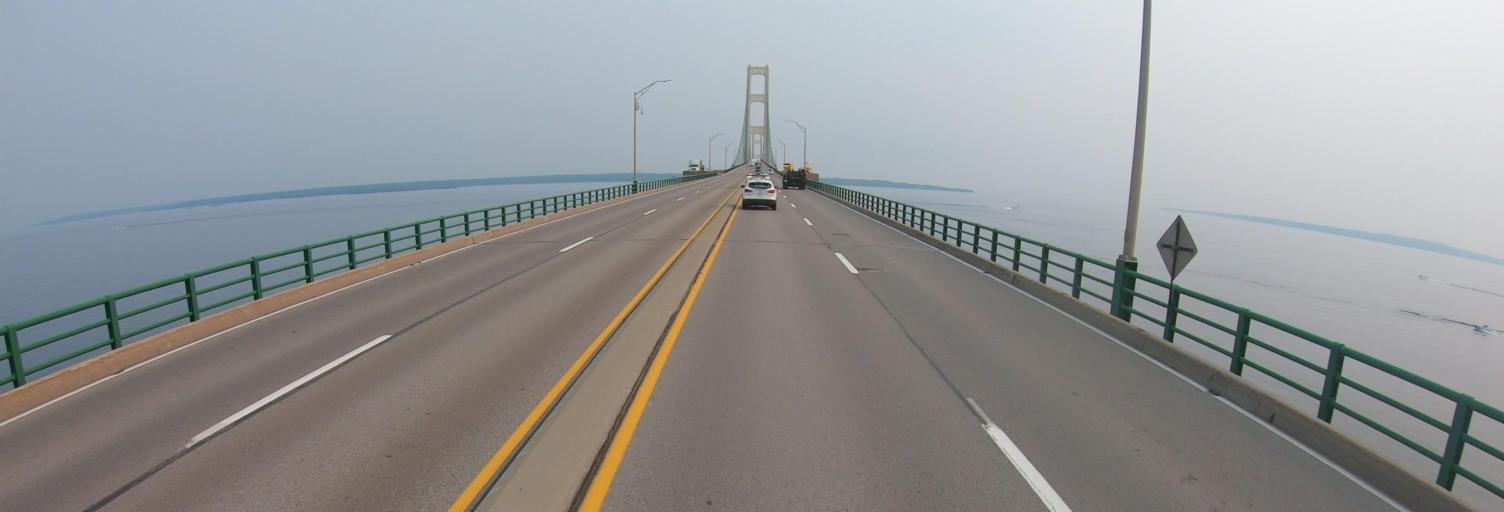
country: US
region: Michigan
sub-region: Mackinac County
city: Saint Ignace
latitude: 45.8019
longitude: -84.7316
